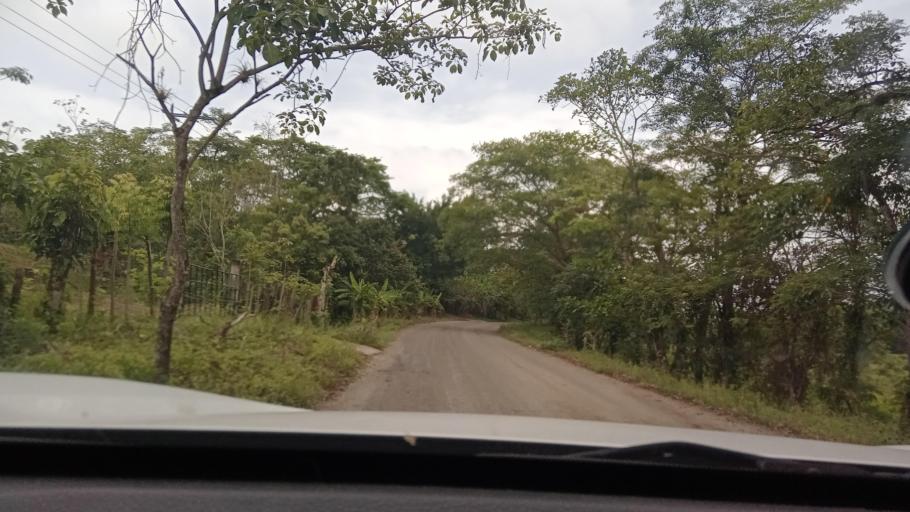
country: MX
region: Tabasco
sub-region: Huimanguillo
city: Francisco Rueda
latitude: 17.5404
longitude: -94.1269
